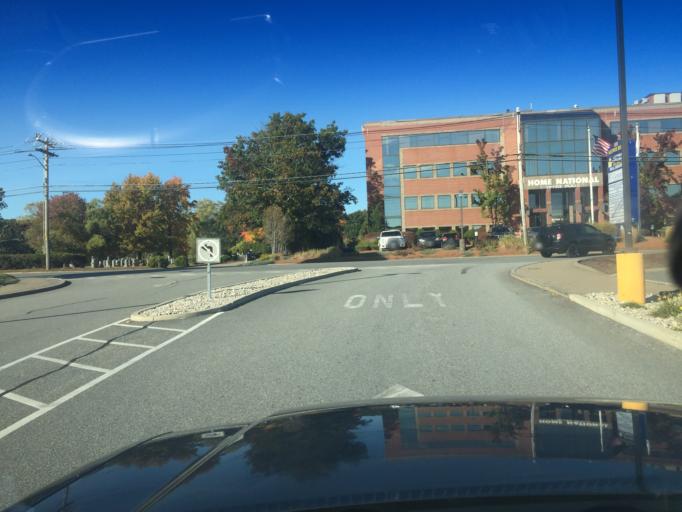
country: US
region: Massachusetts
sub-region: Worcester County
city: Milford
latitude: 42.1478
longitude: -71.4902
